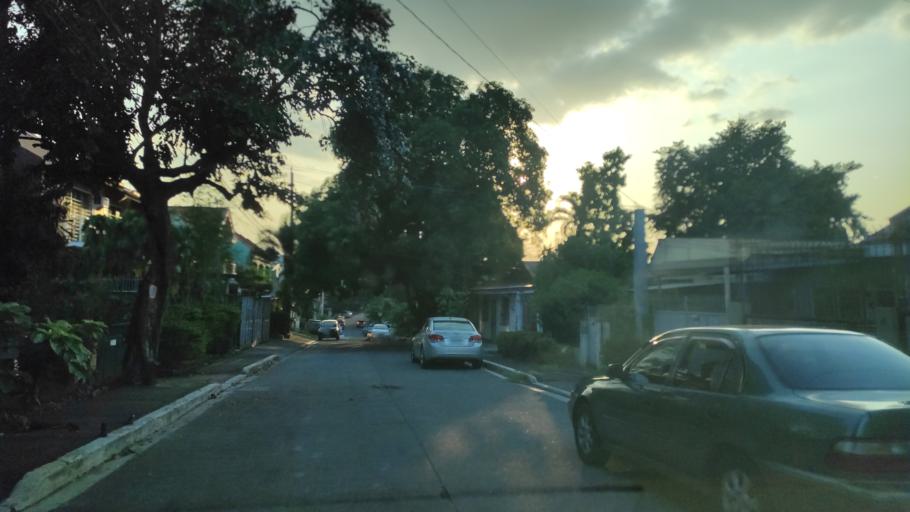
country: PH
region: Calabarzon
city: Bagong Pagasa
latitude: 14.6733
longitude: 121.0219
